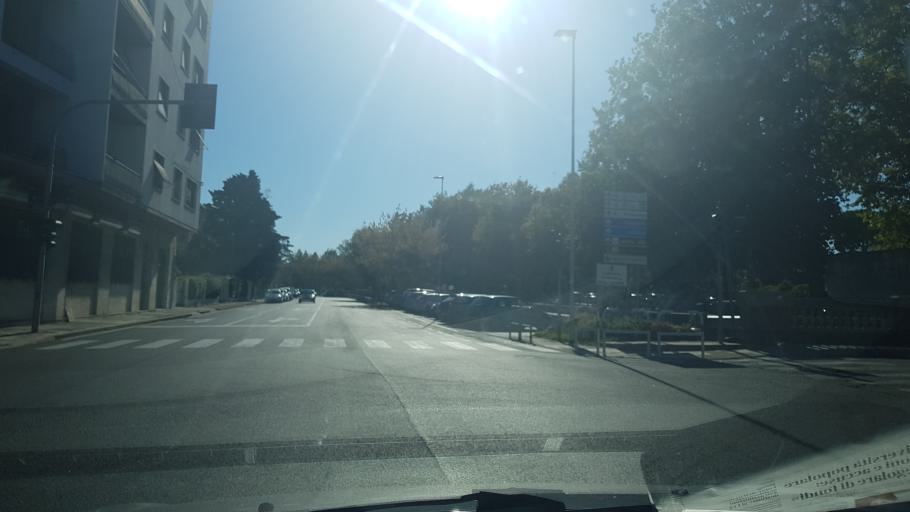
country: IT
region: Friuli Venezia Giulia
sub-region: Provincia di Gorizia
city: Monfalcone
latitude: 45.8064
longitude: 13.5289
